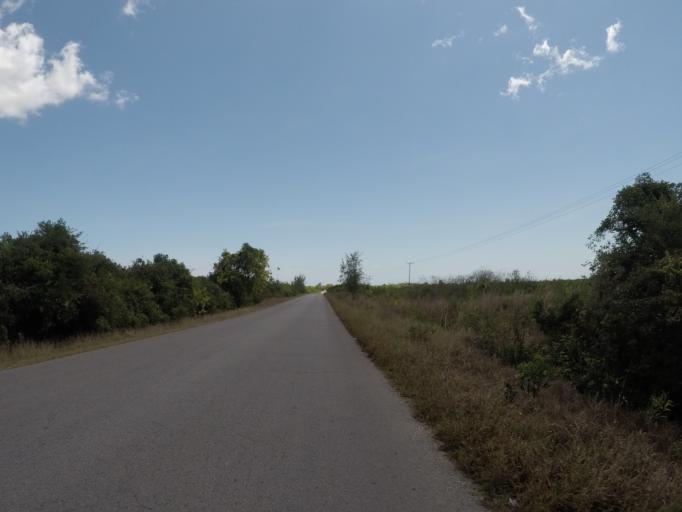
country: TZ
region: Zanzibar Central/South
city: Nganane
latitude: -6.2843
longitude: 39.4602
